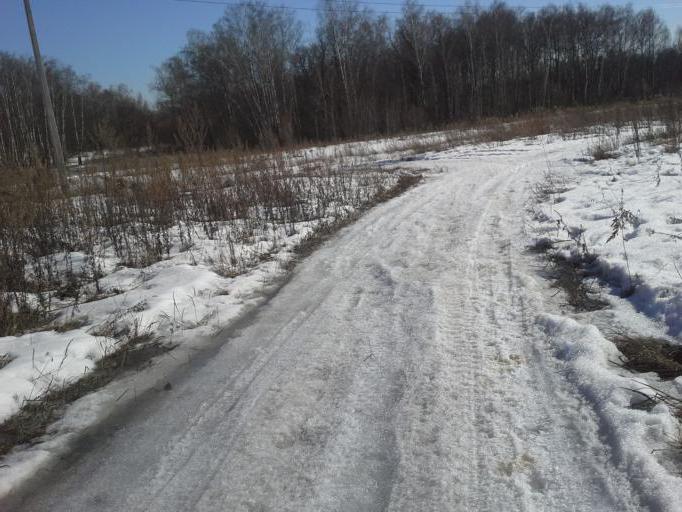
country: RU
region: Moskovskaya
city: Mosrentgen
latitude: 55.5851
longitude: 37.4435
